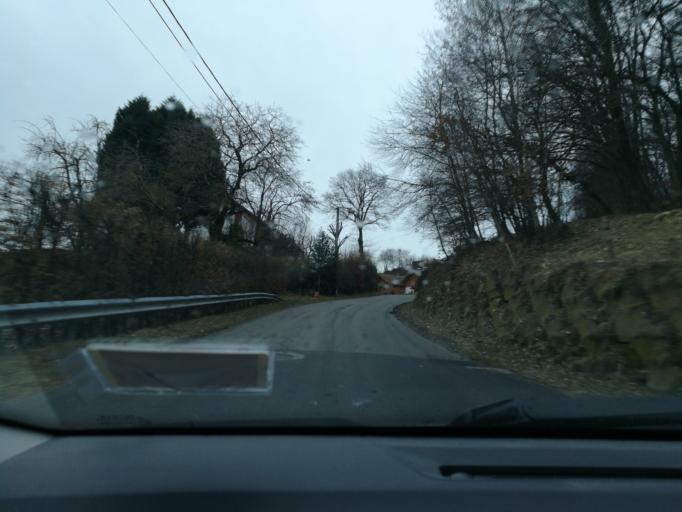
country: FR
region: Rhone-Alpes
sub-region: Departement de la Haute-Savoie
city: Sallanches
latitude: 45.9293
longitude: 6.6290
